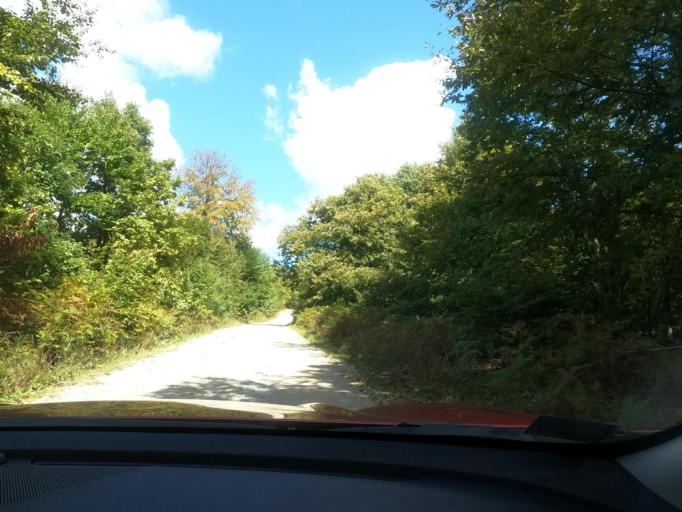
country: HR
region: Karlovacka
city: Vojnic
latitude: 45.2796
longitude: 15.7806
